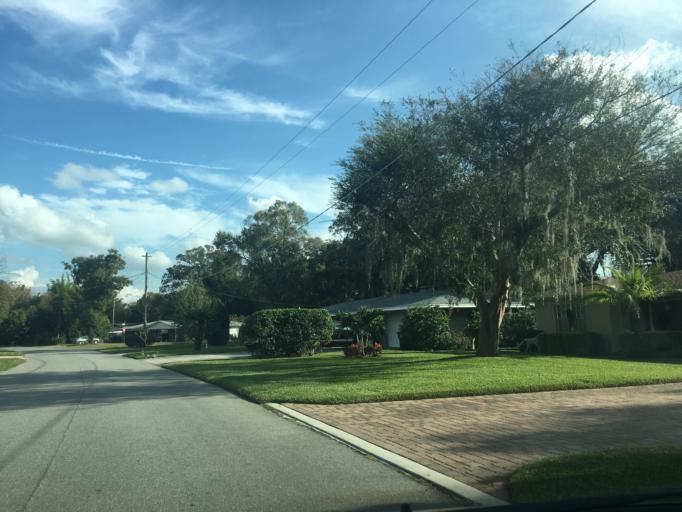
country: US
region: Florida
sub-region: Hillsborough County
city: Egypt Lake-Leto
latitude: 27.9930
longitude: -82.4700
